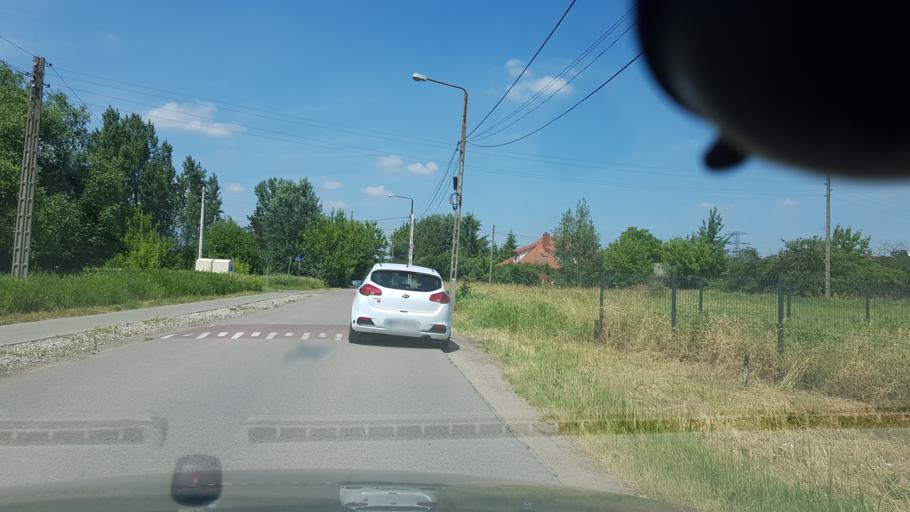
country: PL
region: Masovian Voivodeship
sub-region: Warszawa
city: Targowek
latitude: 52.3031
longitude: 21.0401
